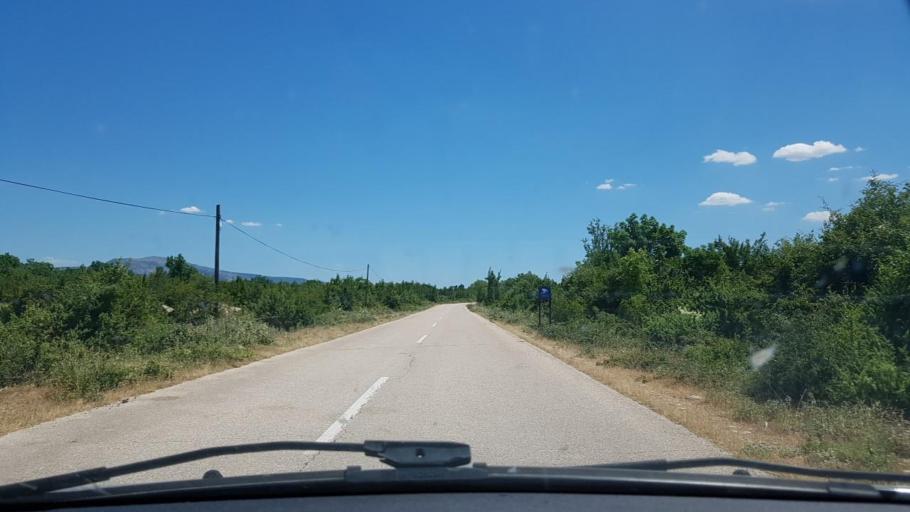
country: HR
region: Sibensko-Kniniska
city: Kistanje
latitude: 43.9688
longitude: 15.9768
